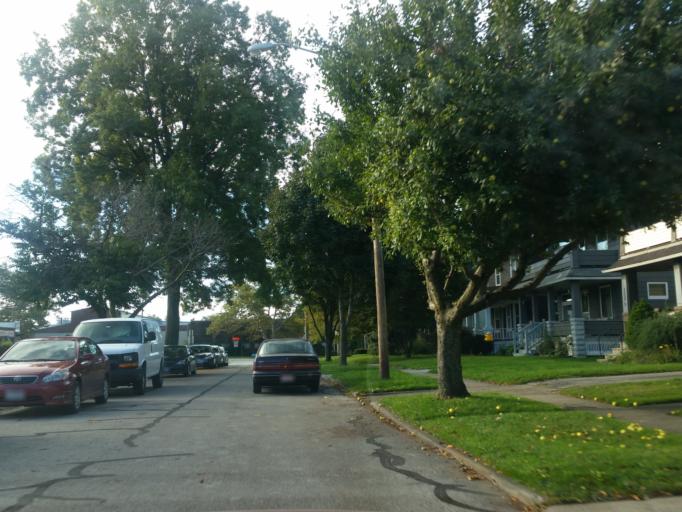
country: US
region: Ohio
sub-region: Cuyahoga County
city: Newburgh Heights
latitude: 41.4492
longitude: -81.6542
